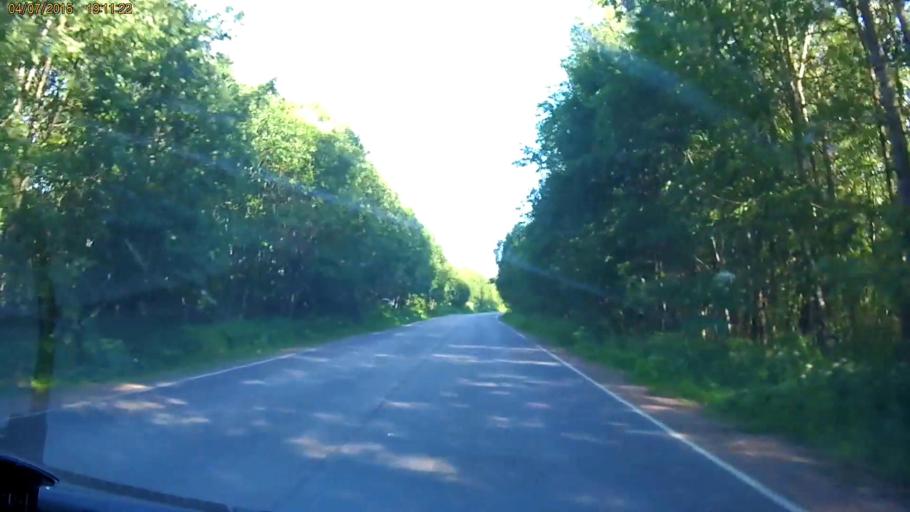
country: RU
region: Leningrad
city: Garbolovo
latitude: 60.3285
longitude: 30.4931
